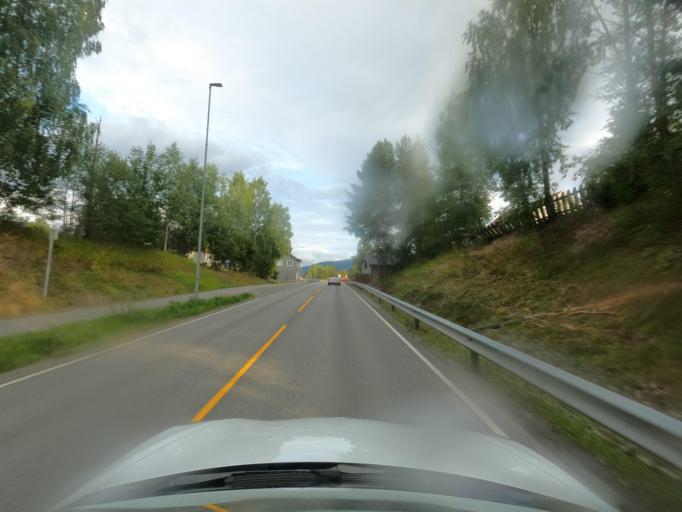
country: NO
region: Telemark
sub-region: Notodden
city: Notodden
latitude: 59.5851
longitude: 9.1618
